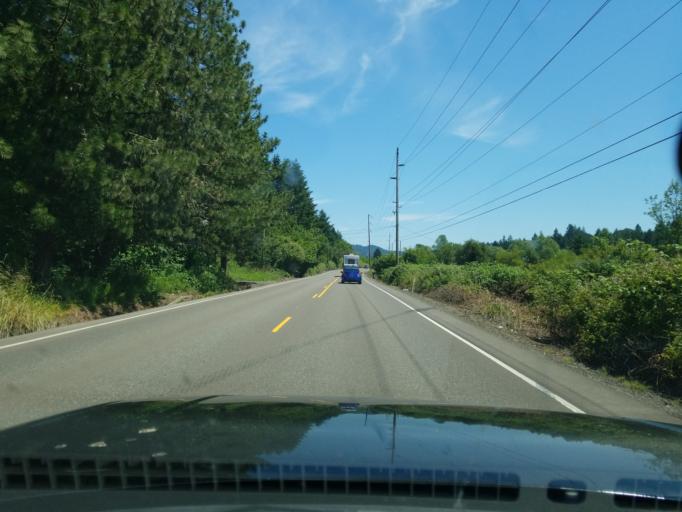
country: US
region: Oregon
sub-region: Yamhill County
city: Yamhill
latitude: 45.3969
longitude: -123.1311
